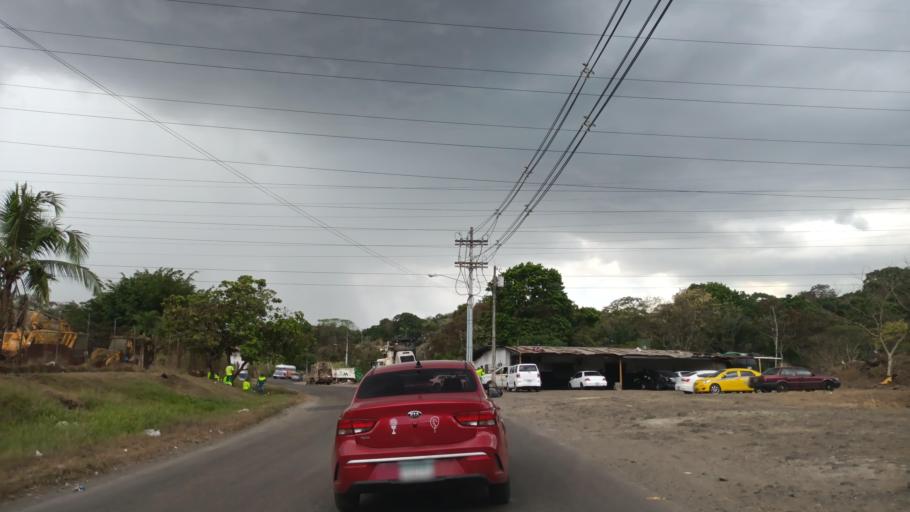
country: PA
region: Panama
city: Las Cumbres
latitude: 9.0462
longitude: -79.5641
